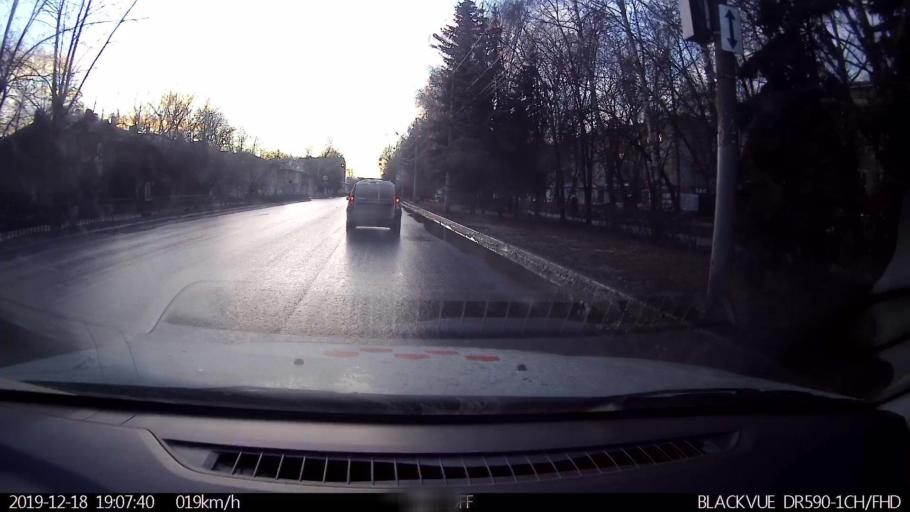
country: RU
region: Nizjnij Novgorod
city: Nizhniy Novgorod
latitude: 56.3208
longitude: 43.8668
